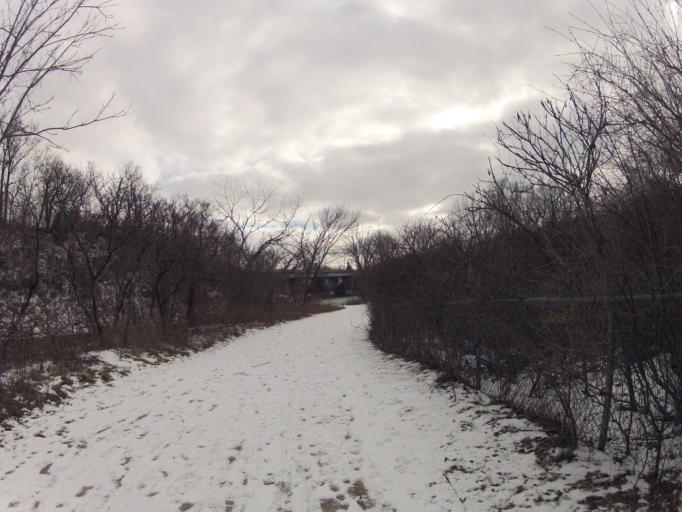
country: CA
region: Ontario
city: Mississauga
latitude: 43.5727
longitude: -79.6933
